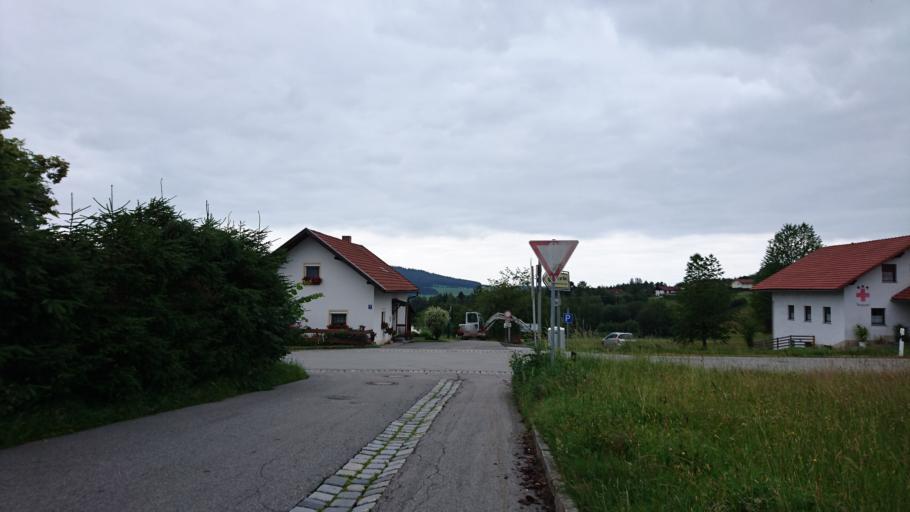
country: DE
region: Bavaria
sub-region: Lower Bavaria
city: Neuschonau
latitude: 48.8828
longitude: 13.4764
